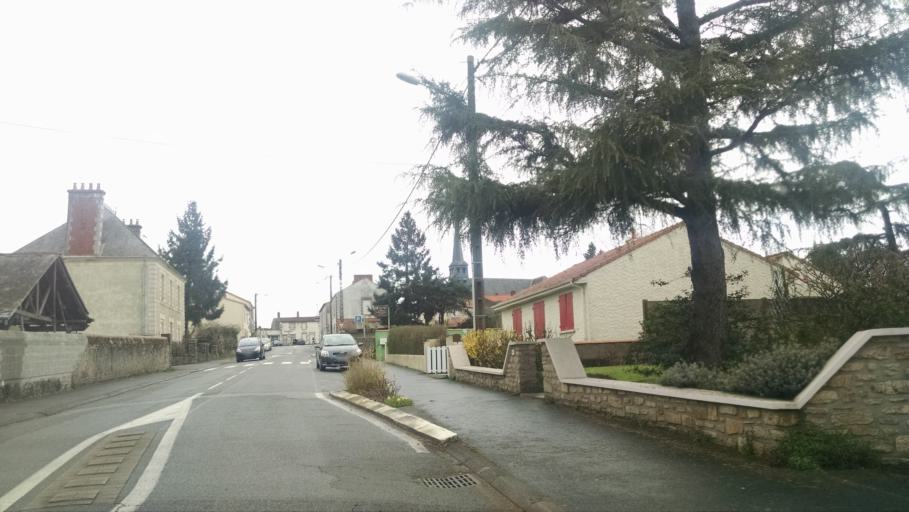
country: FR
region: Pays de la Loire
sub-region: Departement de la Loire-Atlantique
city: Maisdon-sur-Sevre
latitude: 47.0958
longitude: -1.3852
